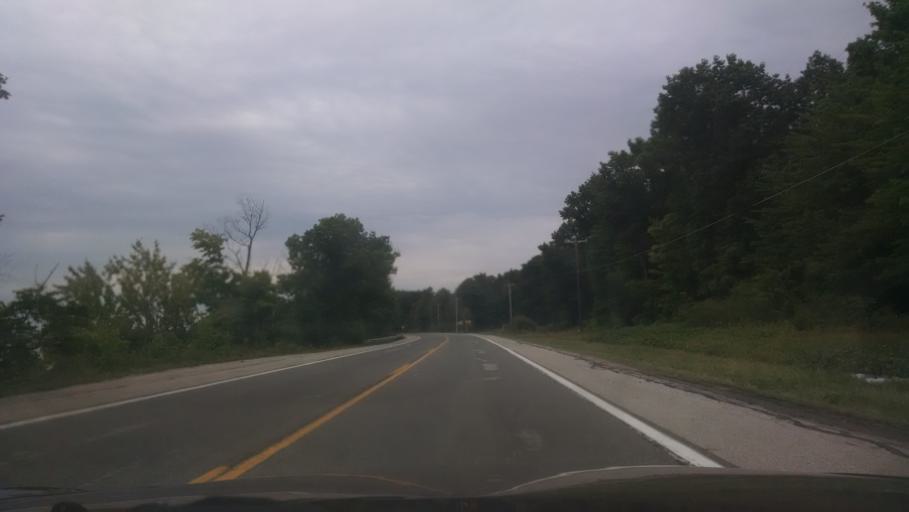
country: US
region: Michigan
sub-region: Leelanau County
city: Greilickville
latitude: 44.8128
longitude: -85.6427
